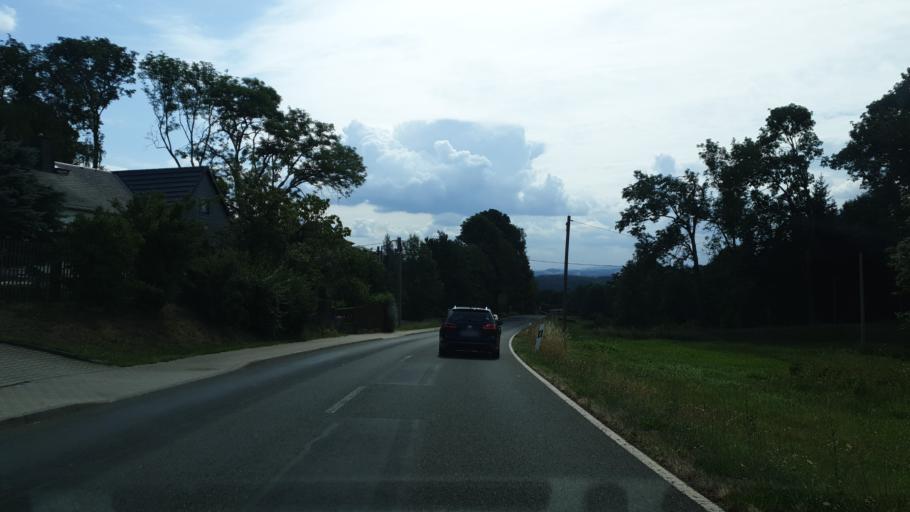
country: DE
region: Saxony
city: Hirschfeld
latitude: 50.6331
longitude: 12.4375
